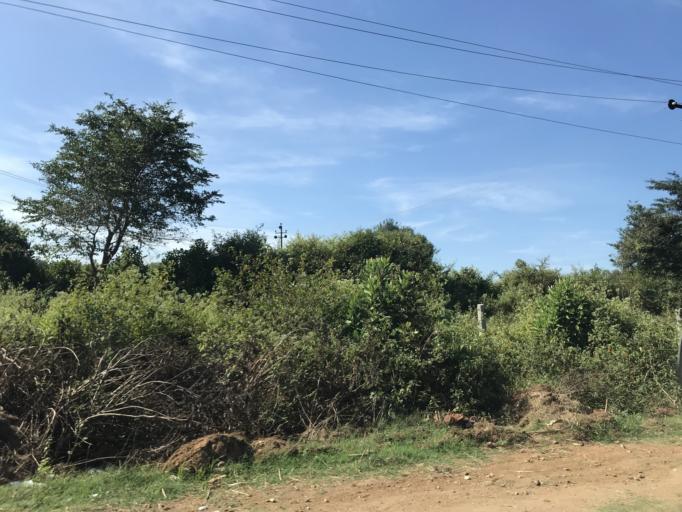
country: IN
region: Karnataka
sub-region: Mysore
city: Sargur
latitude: 12.1216
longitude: 76.4843
